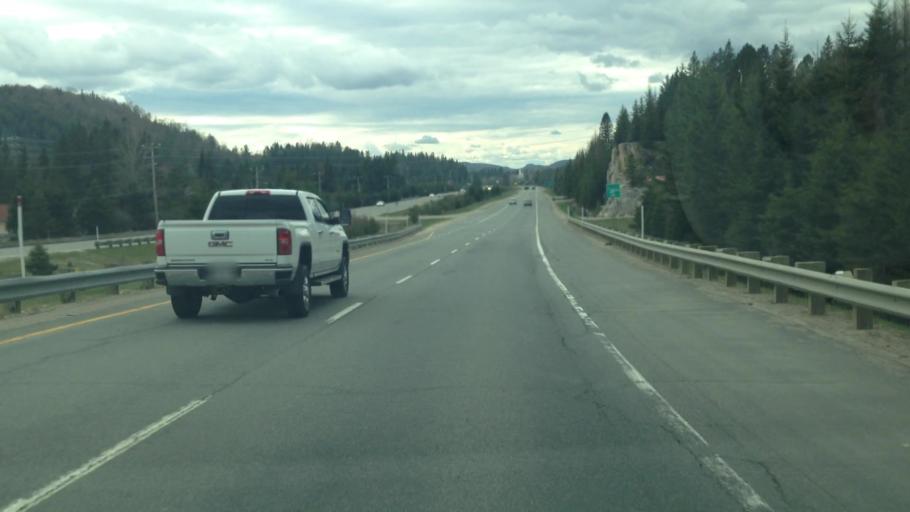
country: CA
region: Quebec
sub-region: Laurentides
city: Mont-Tremblant
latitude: 46.1133
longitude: -74.5400
